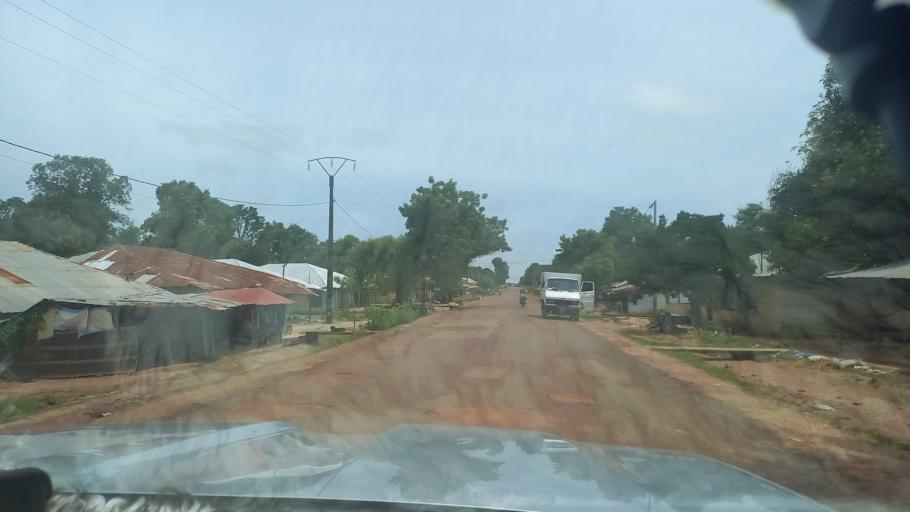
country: SN
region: Kolda
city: Marsassoum
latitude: 12.9674
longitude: -15.9586
